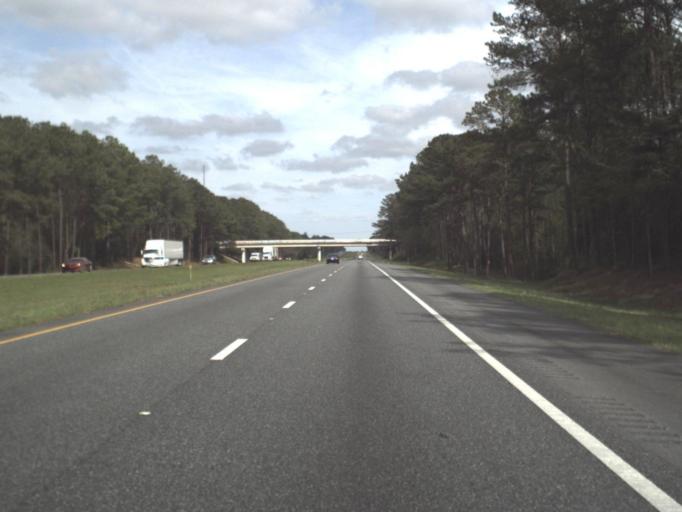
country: US
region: Florida
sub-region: Walton County
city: DeFuniak Springs
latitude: 30.6910
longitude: -86.0768
